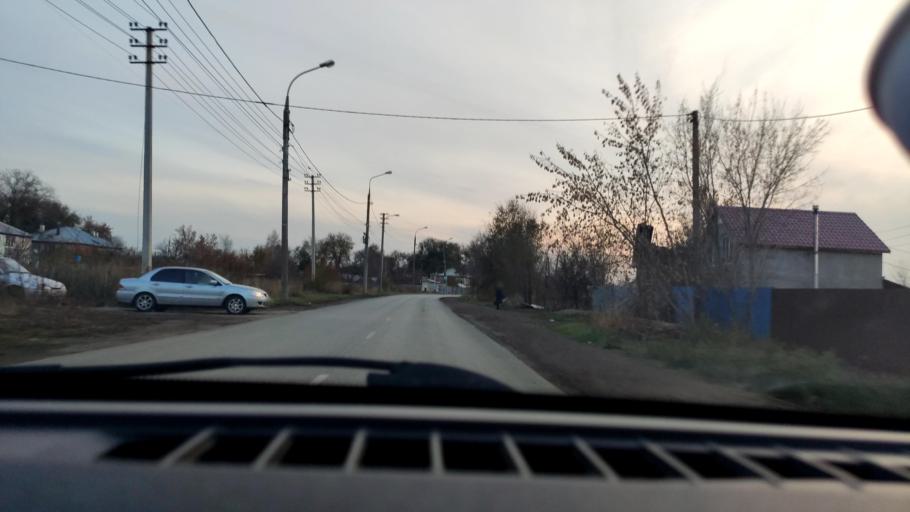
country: RU
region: Samara
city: Samara
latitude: 53.1434
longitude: 50.1331
